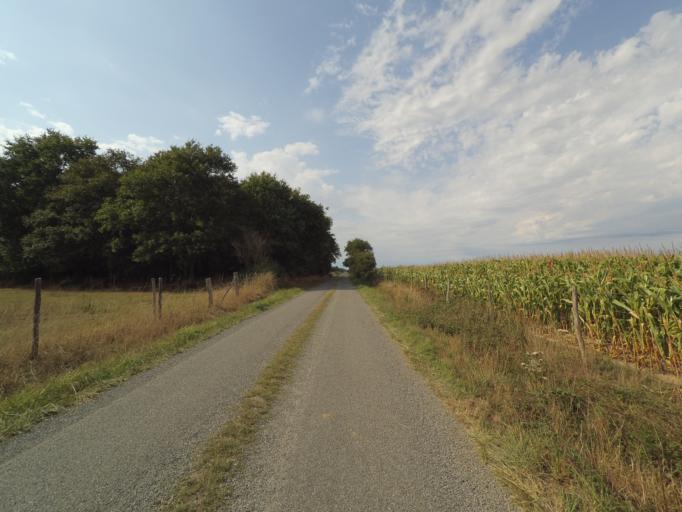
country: FR
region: Pays de la Loire
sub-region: Departement de la Loire-Atlantique
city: Vieillevigne
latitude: 46.9907
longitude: -1.3962
